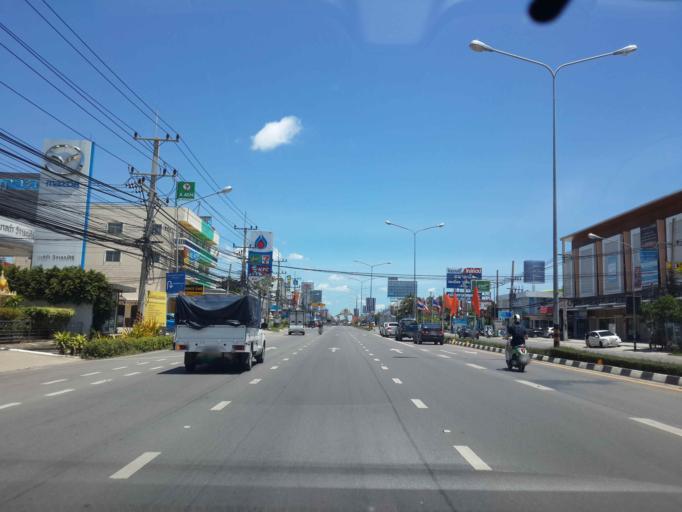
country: TH
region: Prachuap Khiri Khan
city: Hua Hin
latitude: 12.6149
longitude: 99.9503
